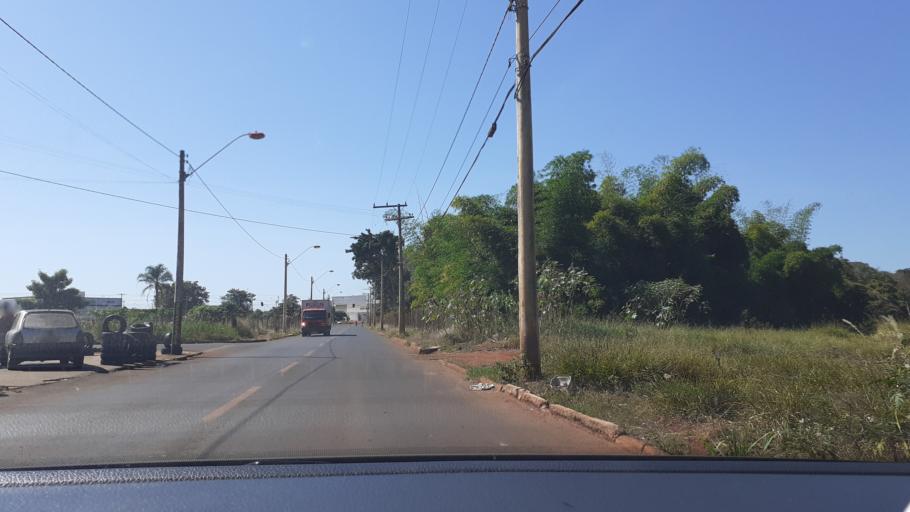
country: BR
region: Goias
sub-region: Itumbiara
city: Itumbiara
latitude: -18.4120
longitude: -49.2509
